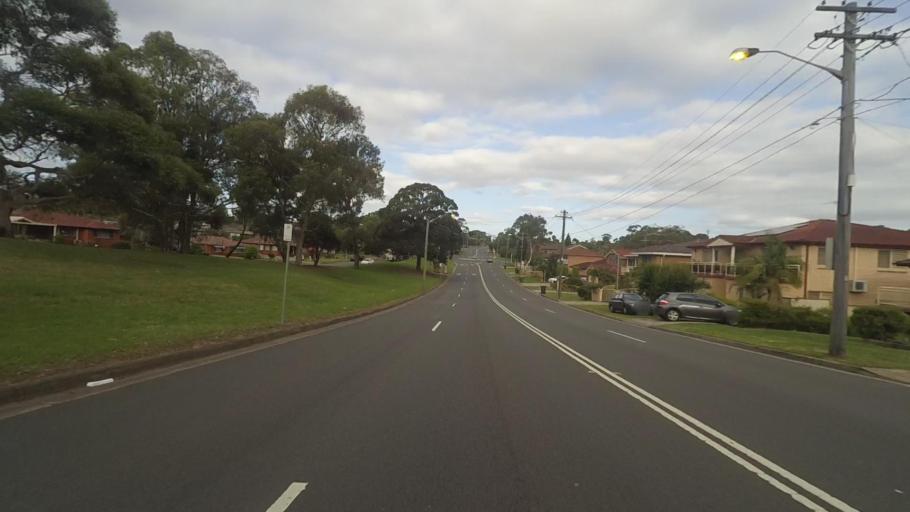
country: AU
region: New South Wales
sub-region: Bankstown
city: Bankstown
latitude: -33.9165
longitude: 151.0041
